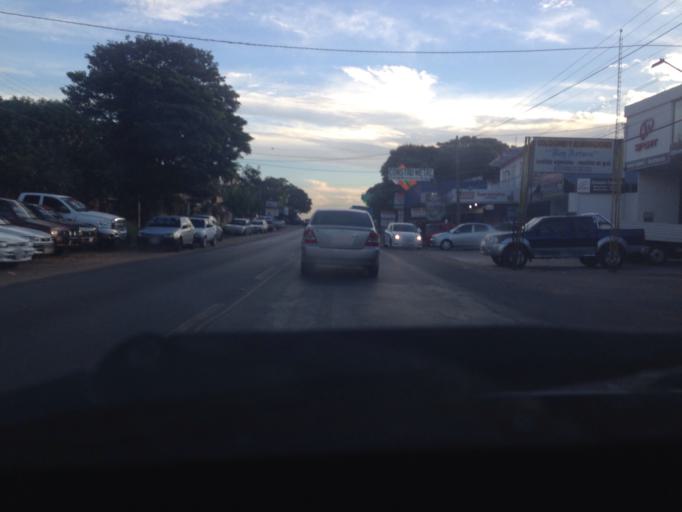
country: PY
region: Central
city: Lambare
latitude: -25.3481
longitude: -57.5900
